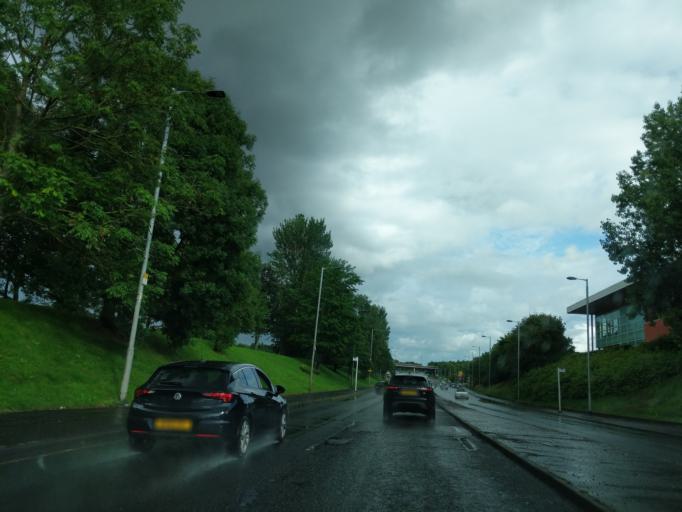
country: GB
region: Scotland
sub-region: East Renfrewshire
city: Newton Mearns
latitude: 55.8069
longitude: -4.3449
